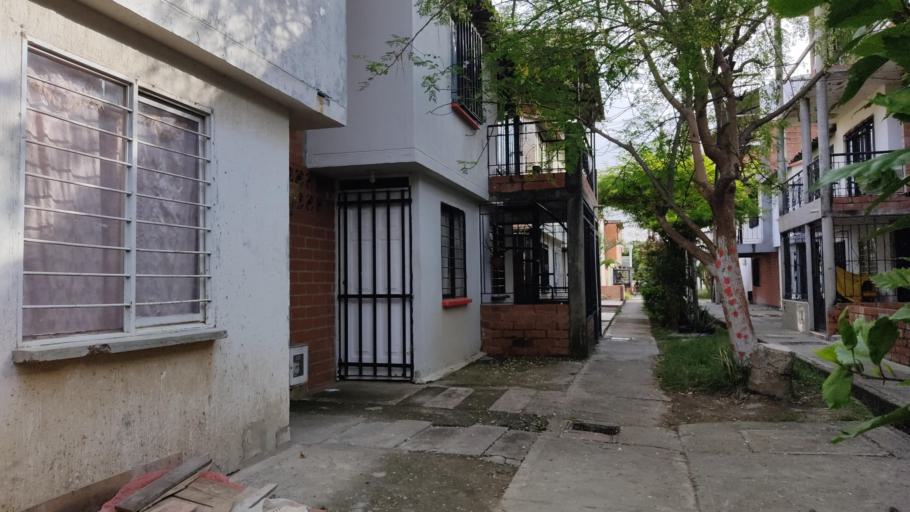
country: CO
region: Valle del Cauca
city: Jamundi
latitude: 3.2391
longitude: -76.5128
